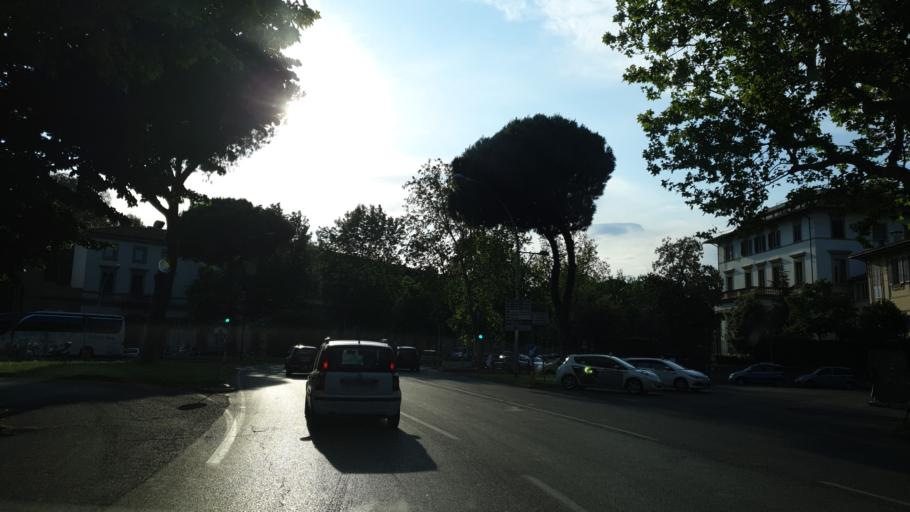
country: IT
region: Tuscany
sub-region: Province of Florence
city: Florence
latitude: 43.7781
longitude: 11.2682
